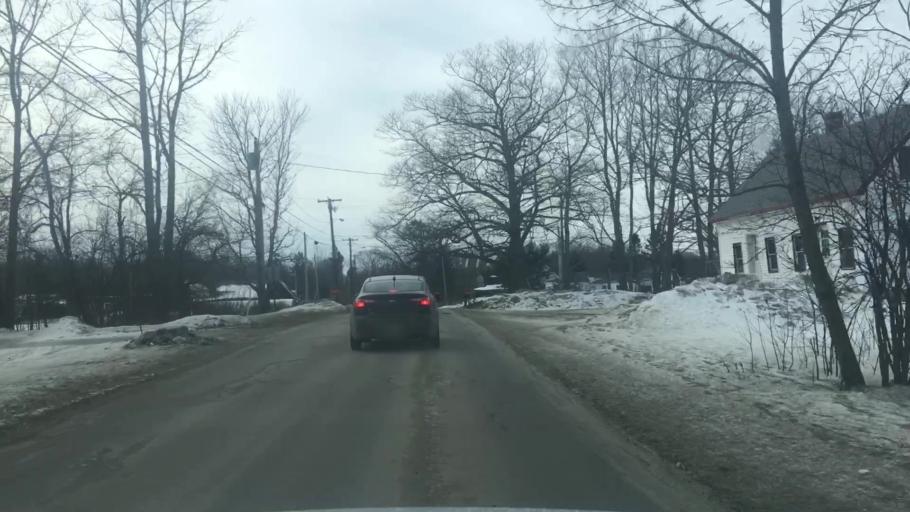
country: US
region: Maine
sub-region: Hancock County
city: Orland
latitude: 44.5744
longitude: -68.7300
